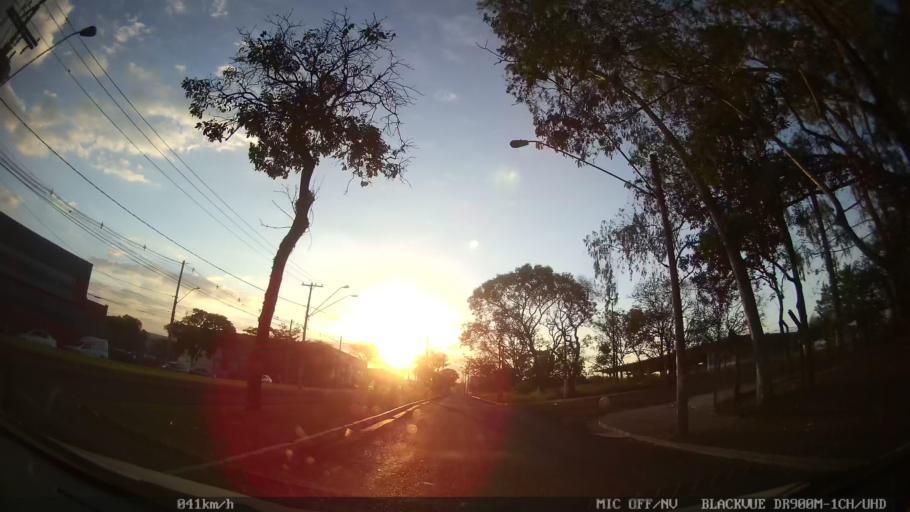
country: BR
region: Sao Paulo
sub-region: Ribeirao Preto
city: Ribeirao Preto
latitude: -21.1503
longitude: -47.7834
